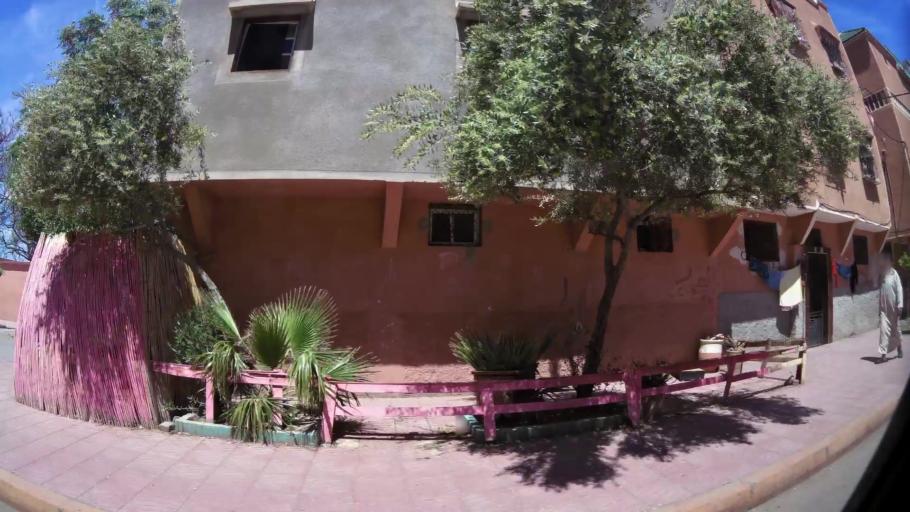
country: MA
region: Marrakech-Tensift-Al Haouz
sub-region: Marrakech
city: Marrakesh
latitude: 31.6564
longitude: -7.9930
